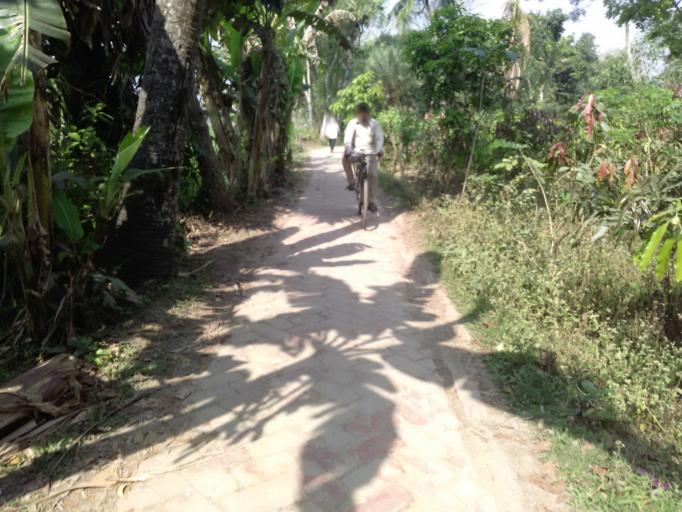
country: BD
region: Khulna
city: Khulna
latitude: 22.8929
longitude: 89.5347
